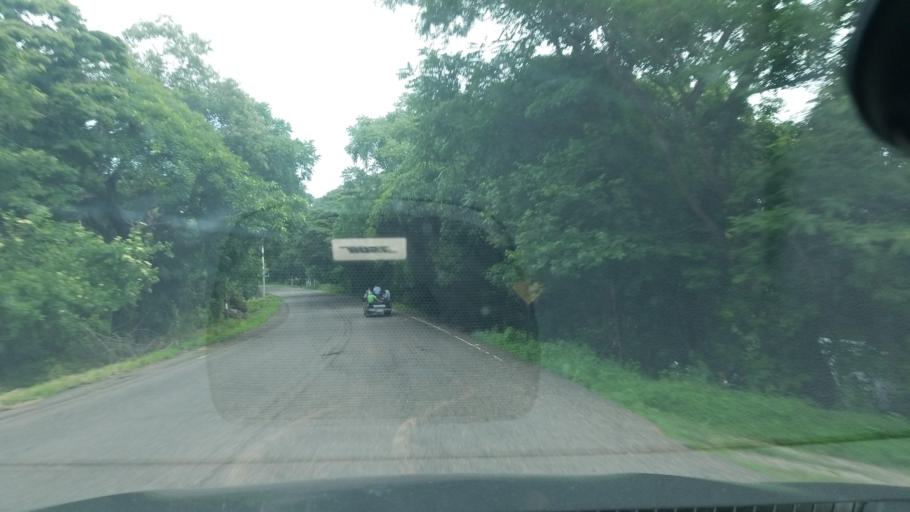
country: HN
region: Choluteca
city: Corpus
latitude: 13.3686
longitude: -87.0268
